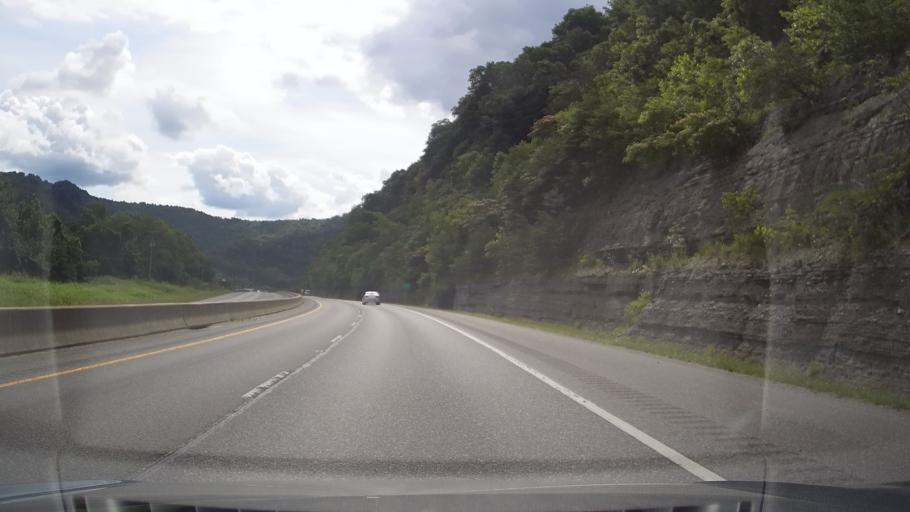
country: US
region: Kentucky
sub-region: Pike County
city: Coal Run Village
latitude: 37.5752
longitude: -82.6490
